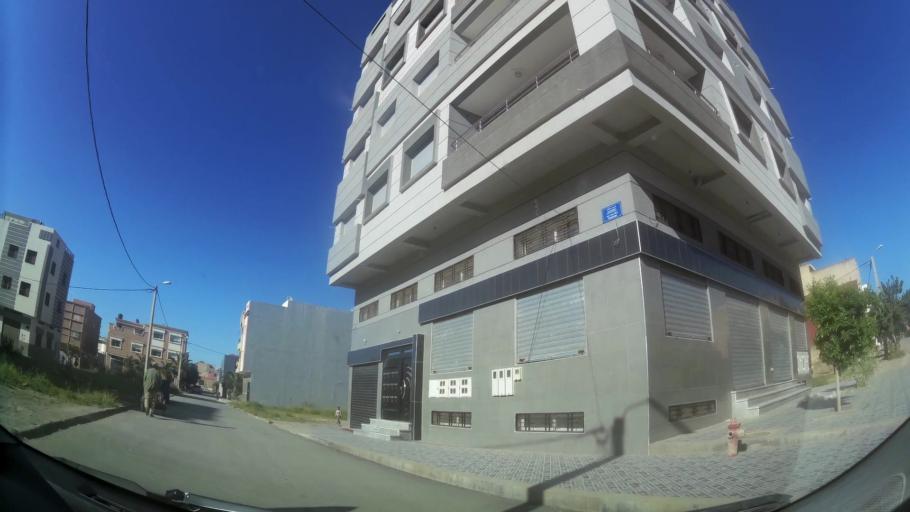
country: MA
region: Oriental
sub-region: Berkane-Taourirt
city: Ahfir
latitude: 34.9551
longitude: -2.1015
